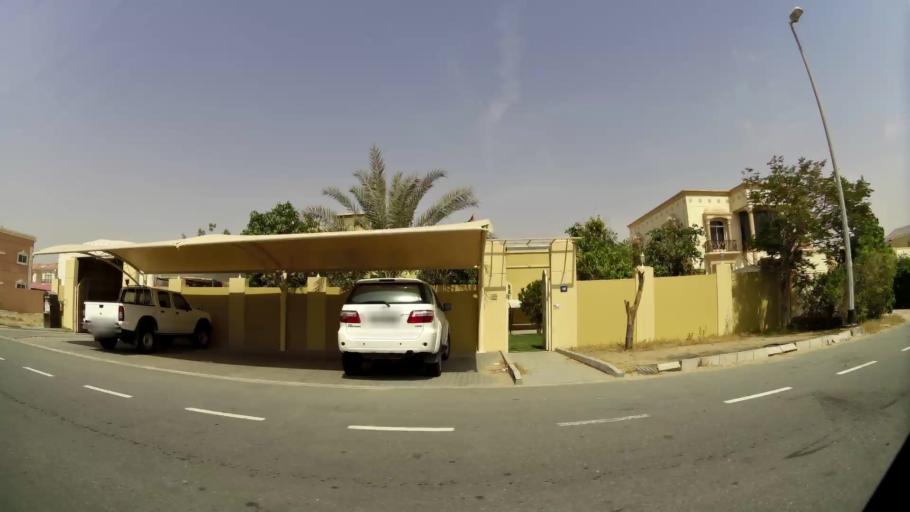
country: AE
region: Ash Shariqah
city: Sharjah
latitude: 25.2394
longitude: 55.4463
